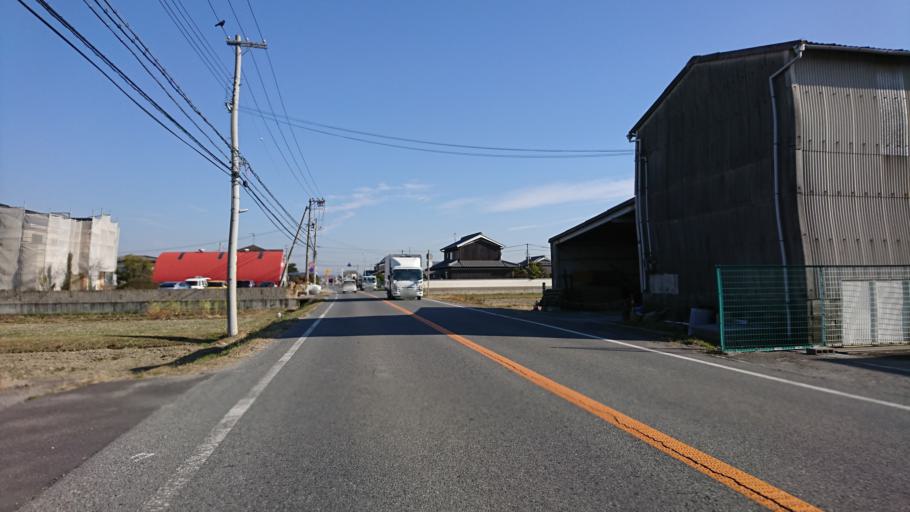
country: JP
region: Hyogo
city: Kakogawacho-honmachi
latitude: 34.7993
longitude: 134.8873
